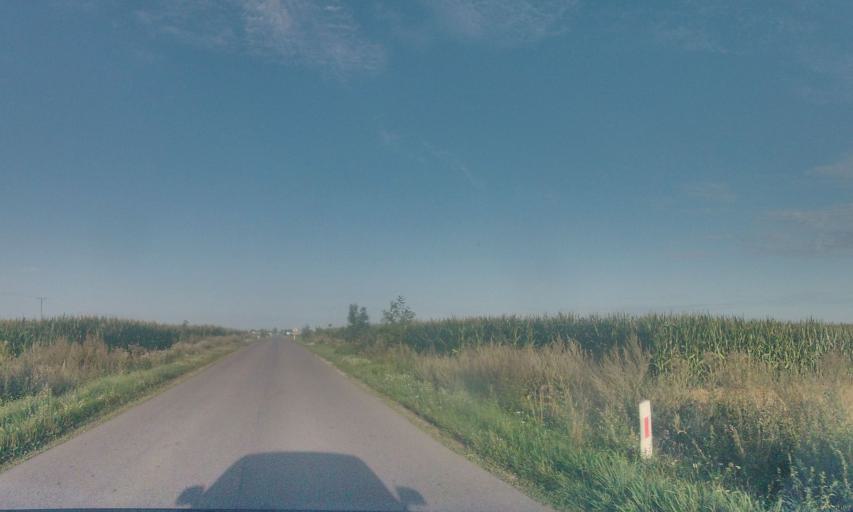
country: PL
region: Masovian Voivodeship
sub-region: Powiat zurominski
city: Zuromin
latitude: 53.0449
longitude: 19.9813
